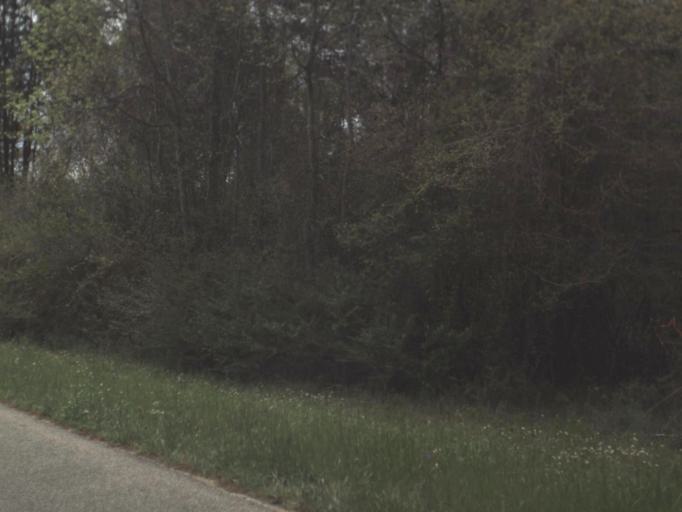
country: US
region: Florida
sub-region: Jackson County
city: Graceville
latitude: 30.8773
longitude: -85.5257
